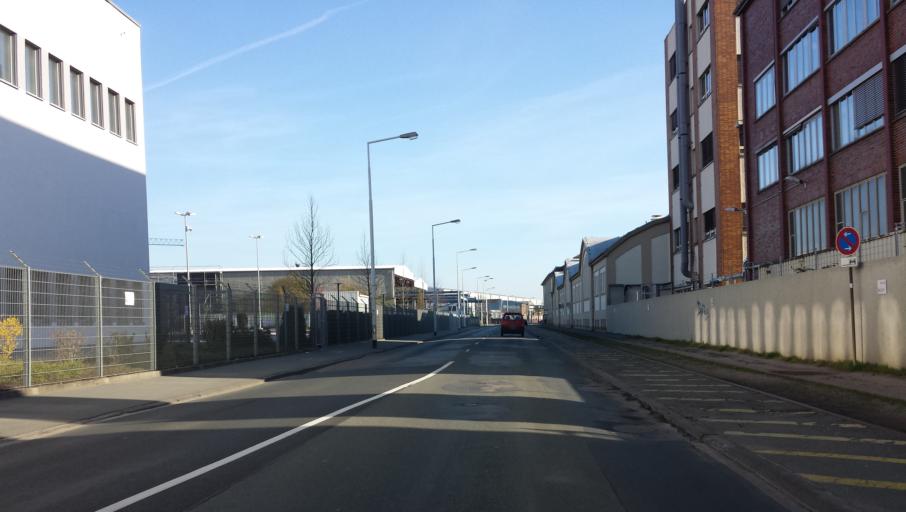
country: DE
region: Hesse
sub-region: Regierungsbezirk Darmstadt
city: Darmstadt
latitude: 49.8770
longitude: 8.6351
